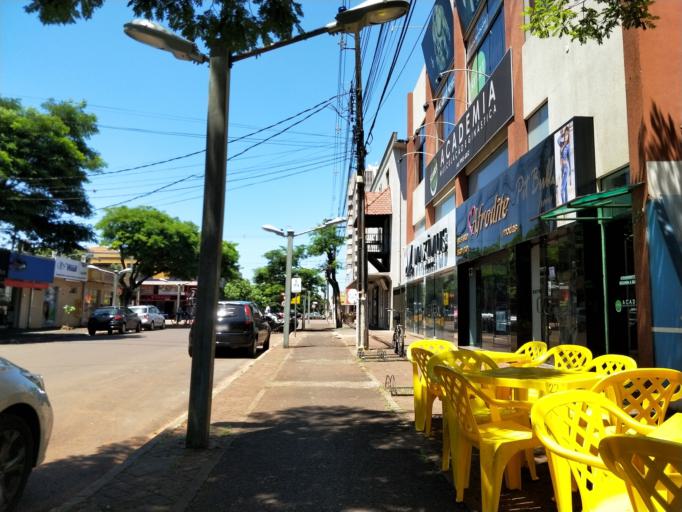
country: BR
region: Parana
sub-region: Marechal Candido Rondon
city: Marechal Candido Rondon
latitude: -24.5628
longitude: -54.0613
